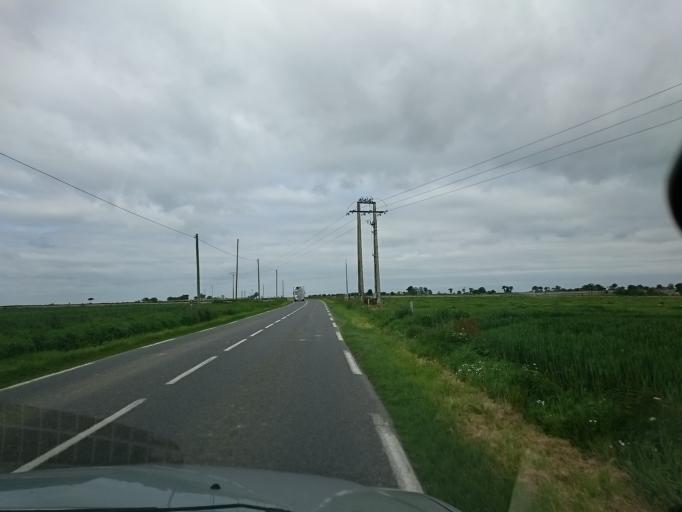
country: FR
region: Lower Normandy
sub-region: Departement de la Manche
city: Saint-James
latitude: 48.5514
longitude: -1.4136
